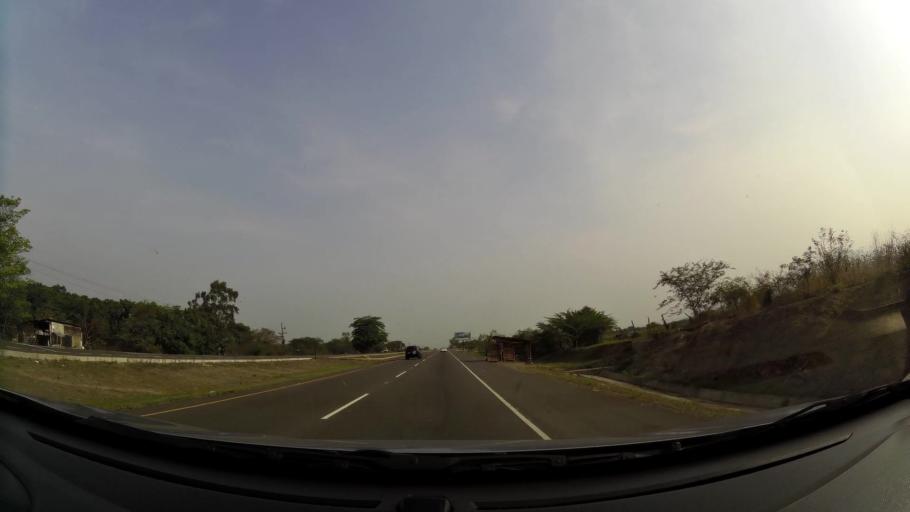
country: HN
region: La Paz
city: Yarumela
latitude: 14.3636
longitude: -87.6022
